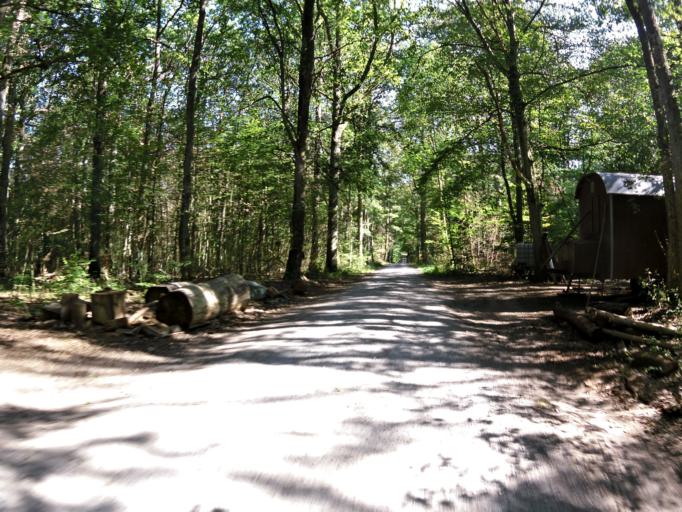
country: DE
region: Bavaria
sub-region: Regierungsbezirk Unterfranken
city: Veitshochheim
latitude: 49.8558
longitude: 9.8785
